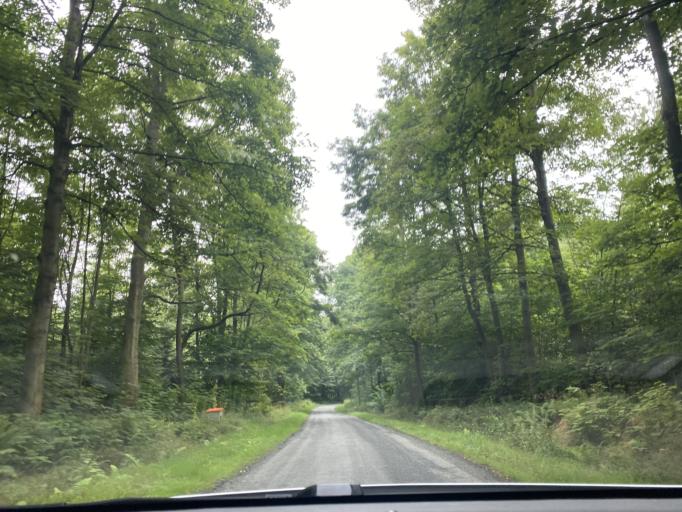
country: DE
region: Saxony
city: Lobau
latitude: 51.0906
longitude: 14.6971
